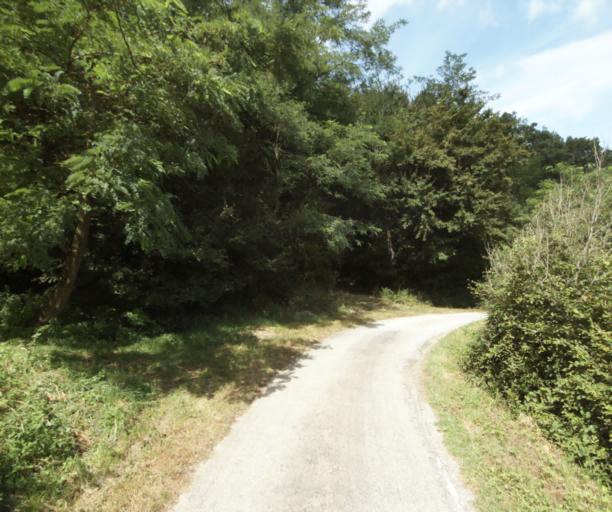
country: FR
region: Midi-Pyrenees
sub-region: Departement du Tarn
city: Dourgne
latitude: 43.4677
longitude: 2.1158
